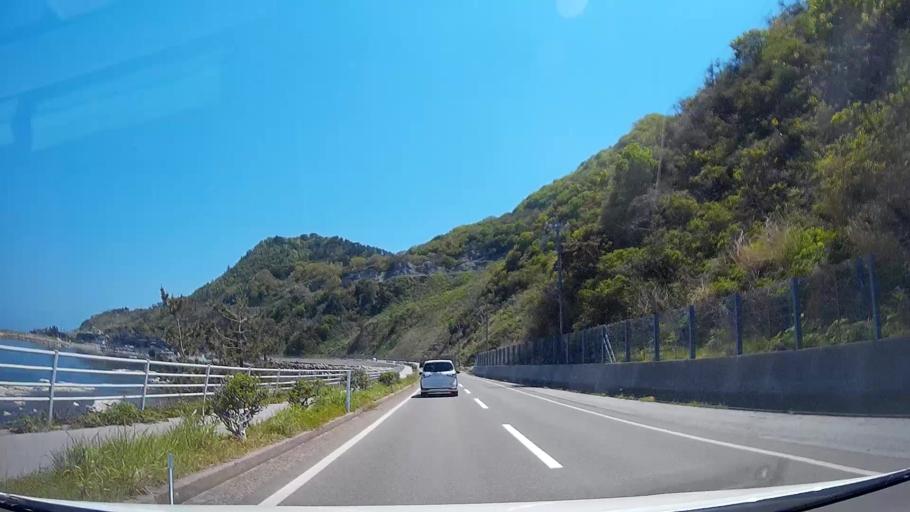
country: JP
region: Ishikawa
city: Nanao
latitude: 37.4798
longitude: 137.1031
